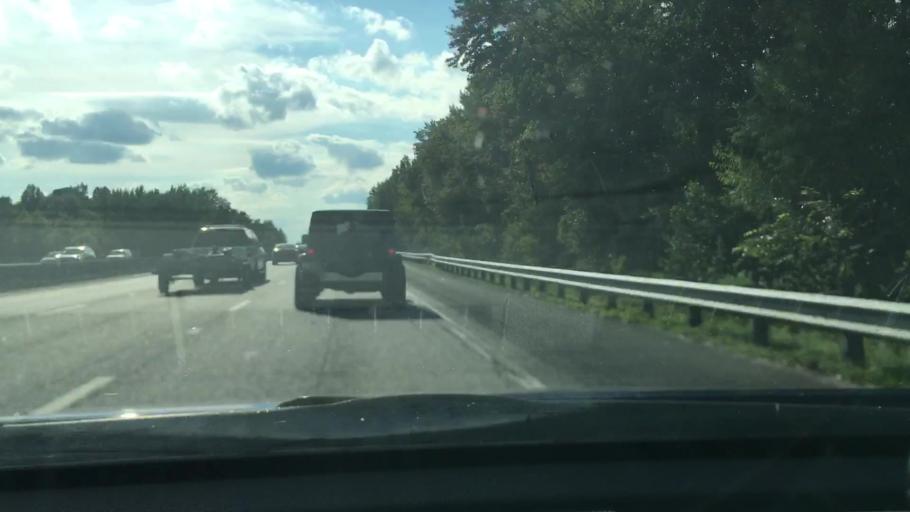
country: US
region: South Carolina
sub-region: Lexington County
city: West Columbia
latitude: 34.0507
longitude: -81.0671
